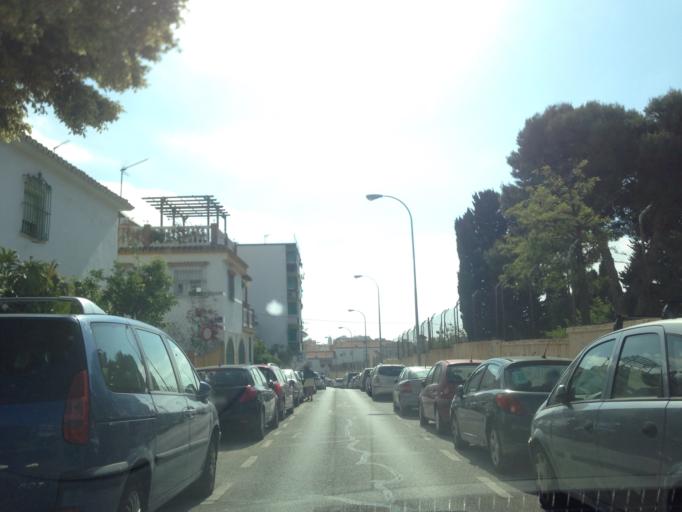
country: ES
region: Andalusia
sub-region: Provincia de Malaga
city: Malaga
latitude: 36.7260
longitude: -4.4408
